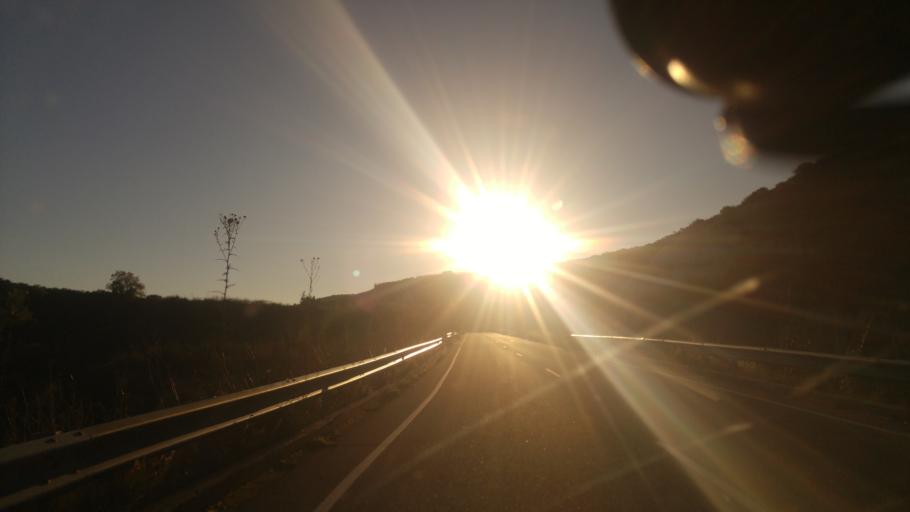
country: CY
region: Limassol
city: Pachna
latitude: 34.8623
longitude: 32.8112
